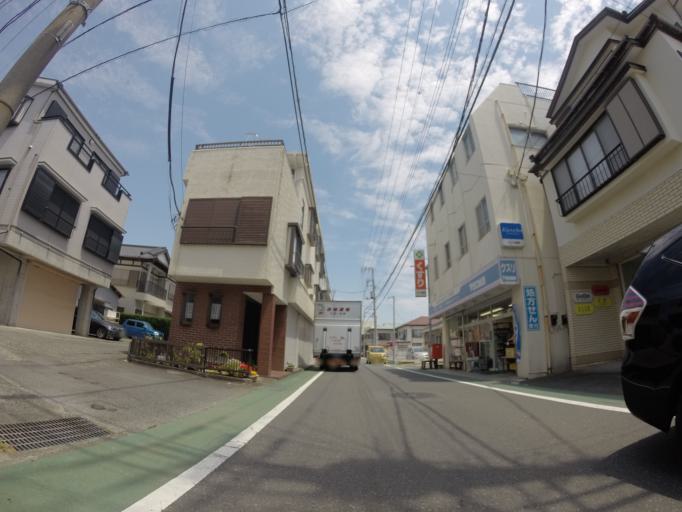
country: JP
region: Shizuoka
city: Shimoda
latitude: 34.7685
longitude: 139.0402
